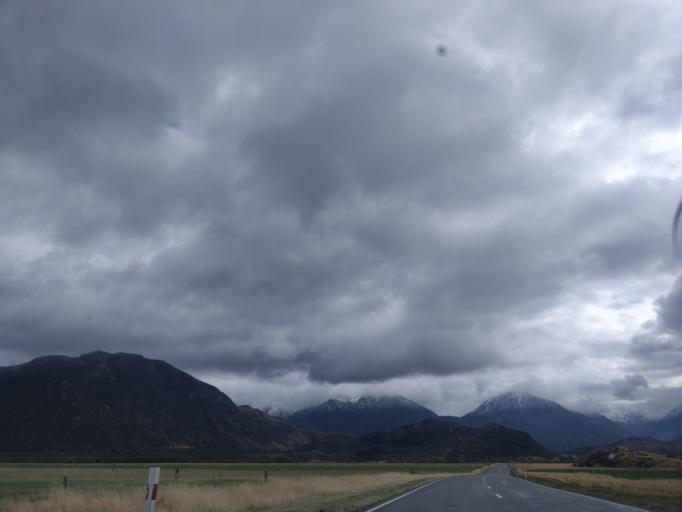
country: NZ
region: Canterbury
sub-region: Waimakariri District
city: Oxford
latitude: -43.0459
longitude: 171.7533
